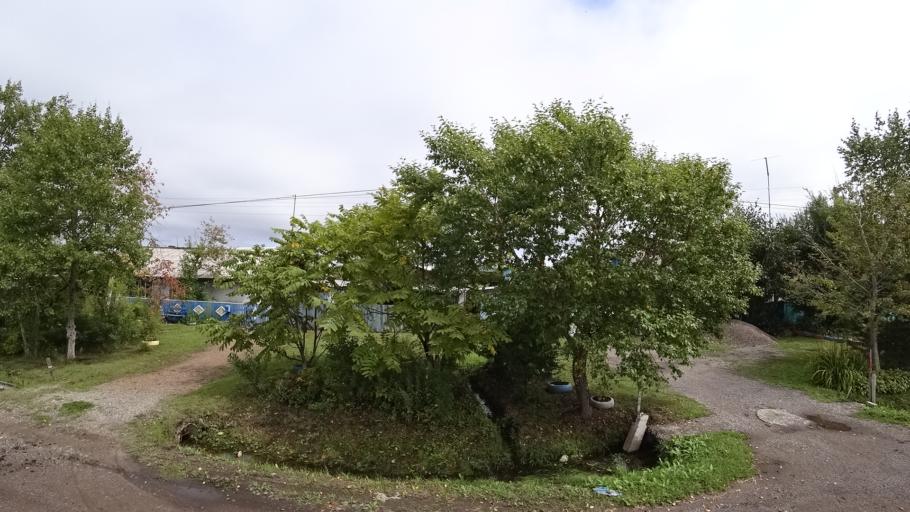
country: RU
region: Primorskiy
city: Monastyrishche
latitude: 44.1985
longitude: 132.4777
